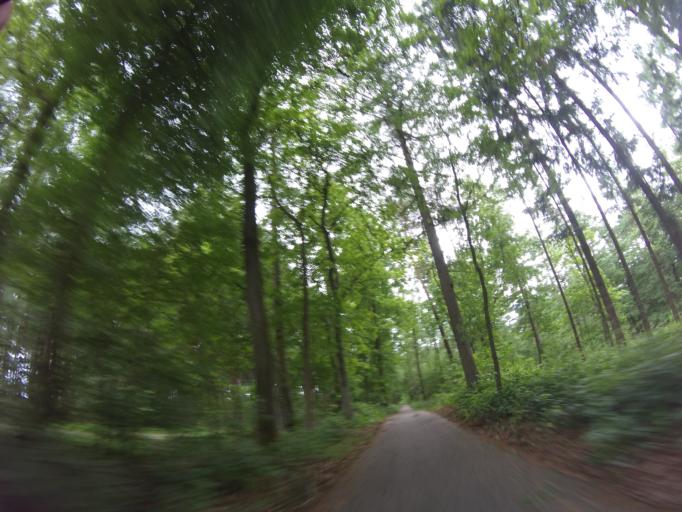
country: NL
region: Drenthe
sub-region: Gemeente Emmen
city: Emmen
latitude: 52.8311
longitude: 6.8764
